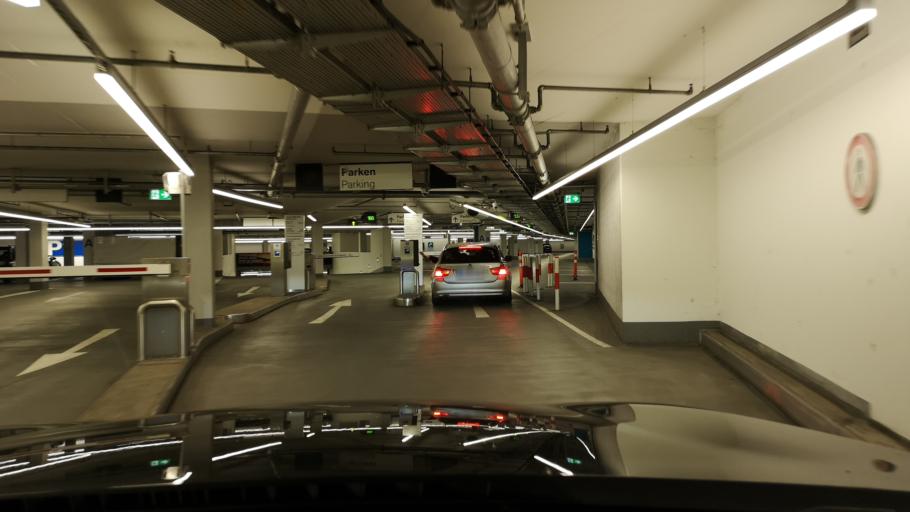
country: DE
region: Bavaria
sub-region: Upper Bavaria
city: Munich
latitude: 48.1779
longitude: 11.5559
